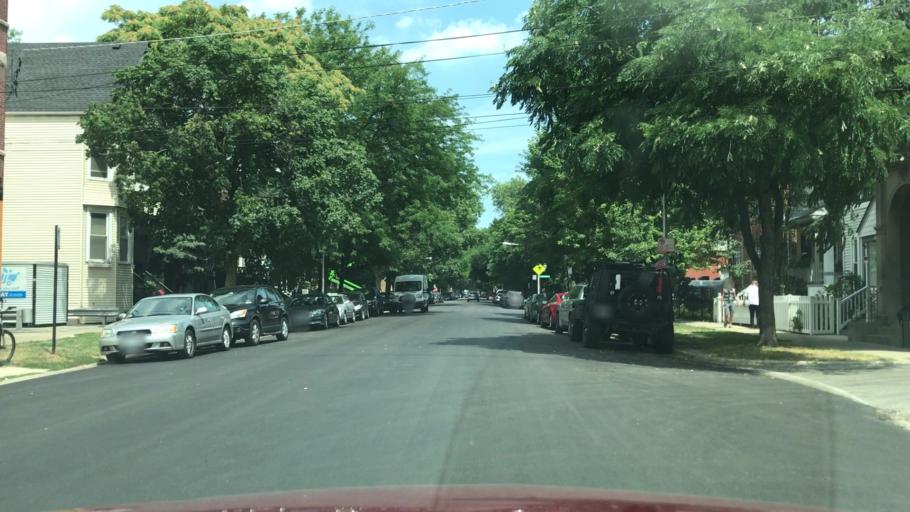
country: US
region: Illinois
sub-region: Cook County
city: Chicago
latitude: 41.9328
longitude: -87.6585
